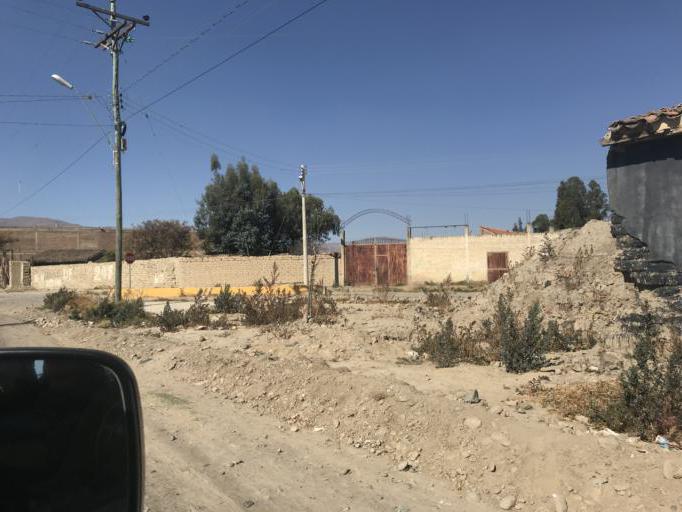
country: BO
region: Cochabamba
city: Punata
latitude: -17.5522
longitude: -65.8515
